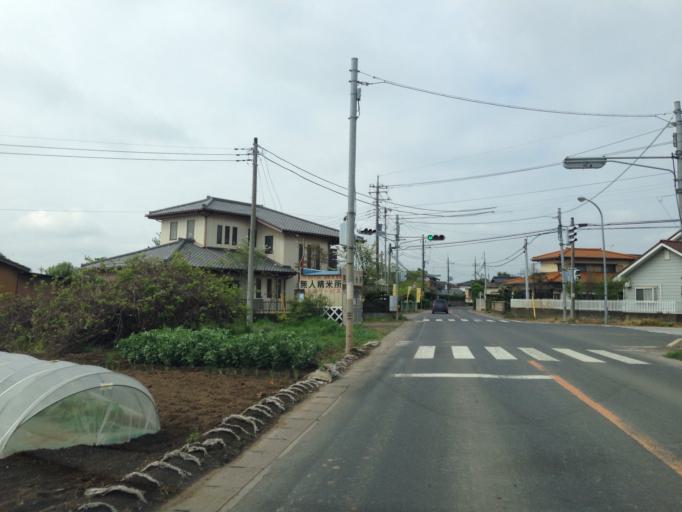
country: JP
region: Ibaraki
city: Ishige
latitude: 36.1608
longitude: 139.9064
